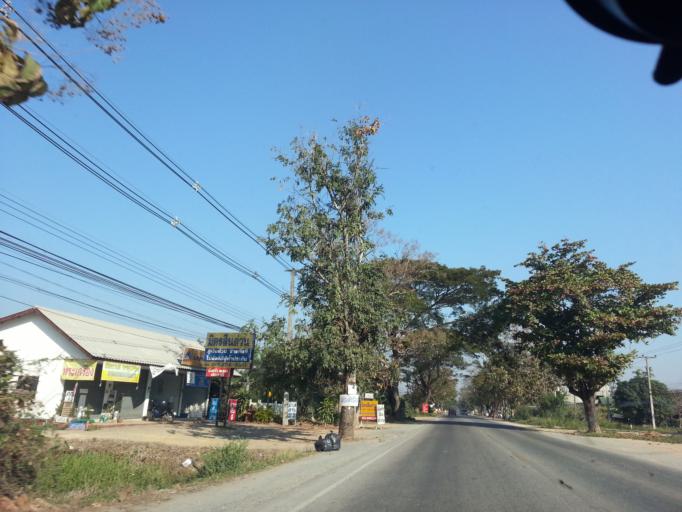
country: TH
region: Chiang Mai
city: San Sai
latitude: 18.9684
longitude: 98.9834
